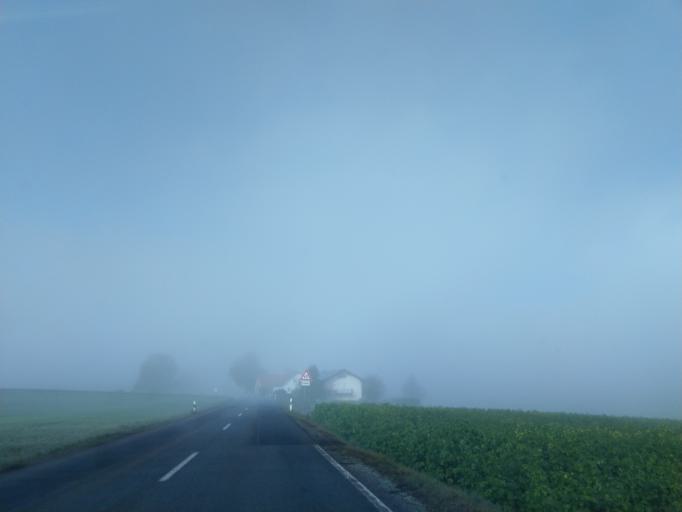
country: DE
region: Bavaria
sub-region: Lower Bavaria
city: Aussernzell
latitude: 48.7259
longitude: 13.1975
